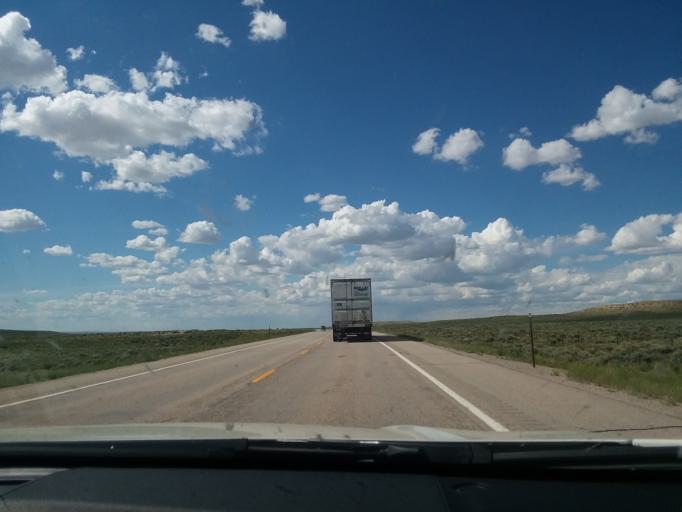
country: US
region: Wyoming
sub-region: Sweetwater County
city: North Rock Springs
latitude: 41.8943
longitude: -109.3545
